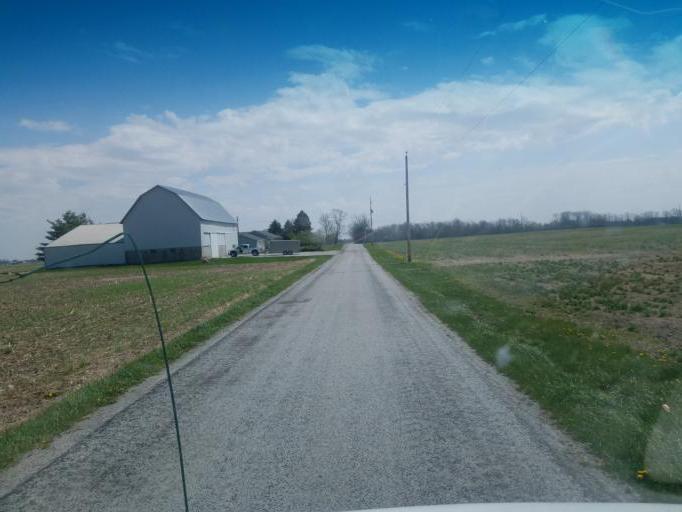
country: US
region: Ohio
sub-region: Hardin County
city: Kenton
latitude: 40.6803
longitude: -83.5505
